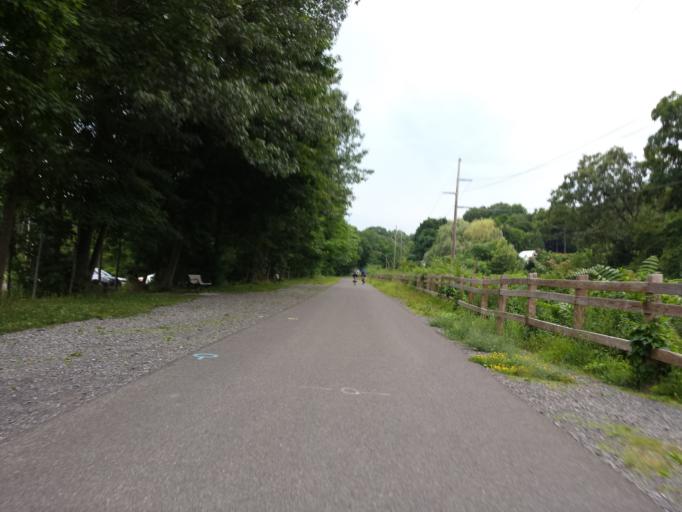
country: US
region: New York
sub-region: Ulster County
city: Highland
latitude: 41.7106
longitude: -73.9568
